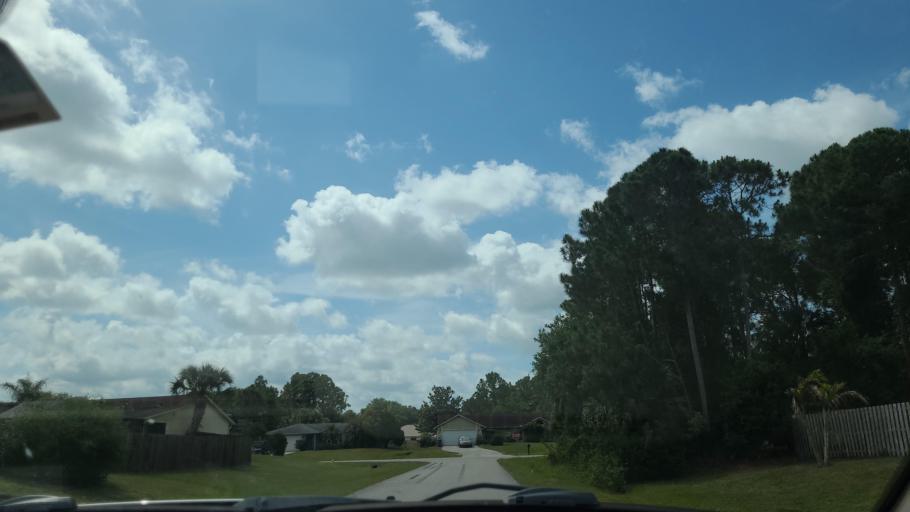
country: US
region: Florida
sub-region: Brevard County
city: Grant-Valkaria
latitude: 27.9681
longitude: -80.6627
